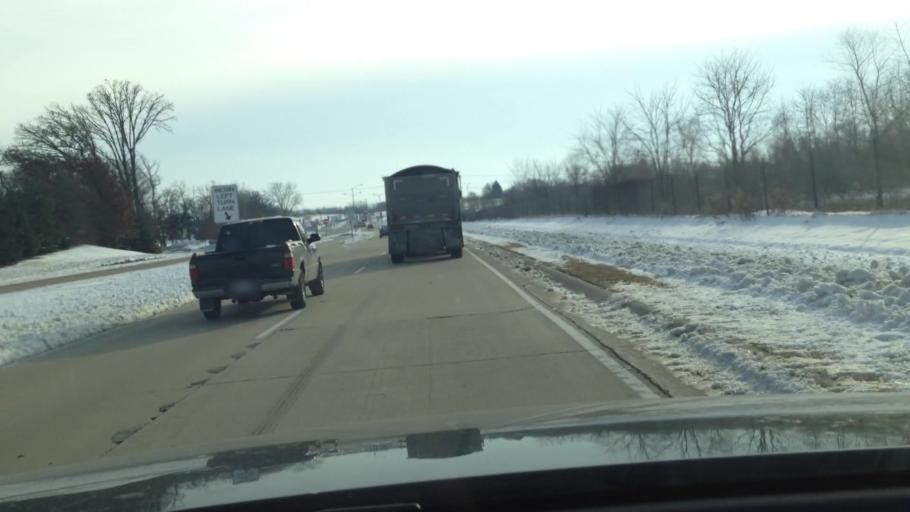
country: US
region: Wisconsin
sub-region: Walworth County
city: Lake Geneva
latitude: 42.5674
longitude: -88.4136
